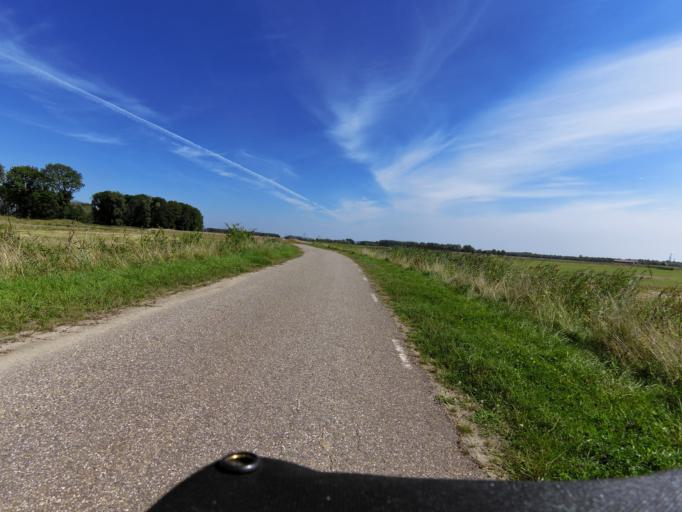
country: NL
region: South Holland
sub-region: Gemeente Sliedrecht
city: Sliedrecht
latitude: 51.7724
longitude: 4.8178
